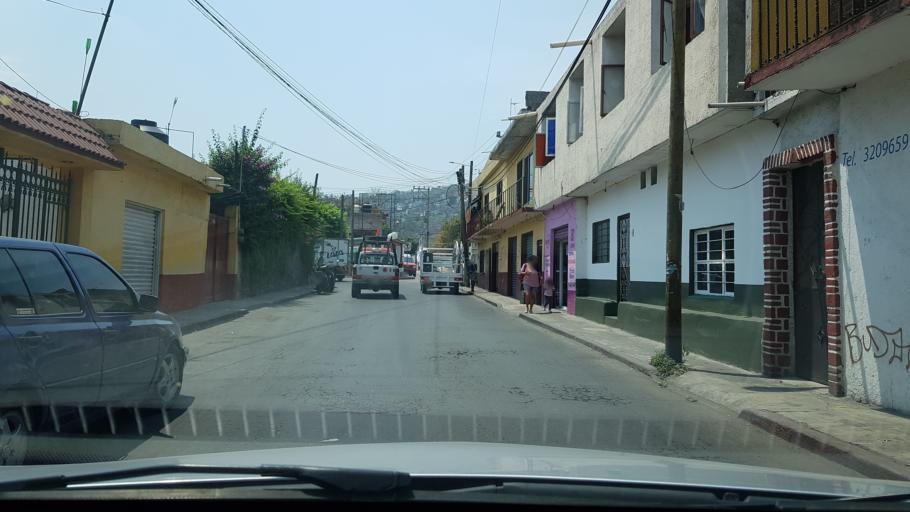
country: MX
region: Morelos
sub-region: Jiutepec
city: Jiutepec
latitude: 18.8797
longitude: -99.1789
